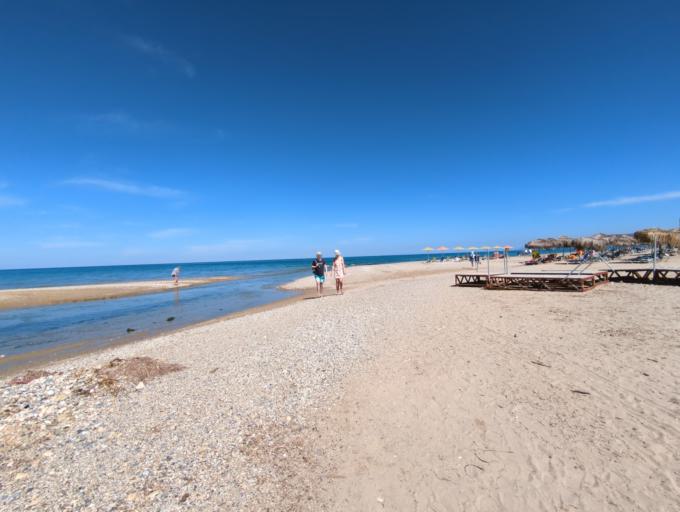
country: GR
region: Crete
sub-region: Nomos Chanias
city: Georgioupolis
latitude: 35.3595
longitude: 24.2668
